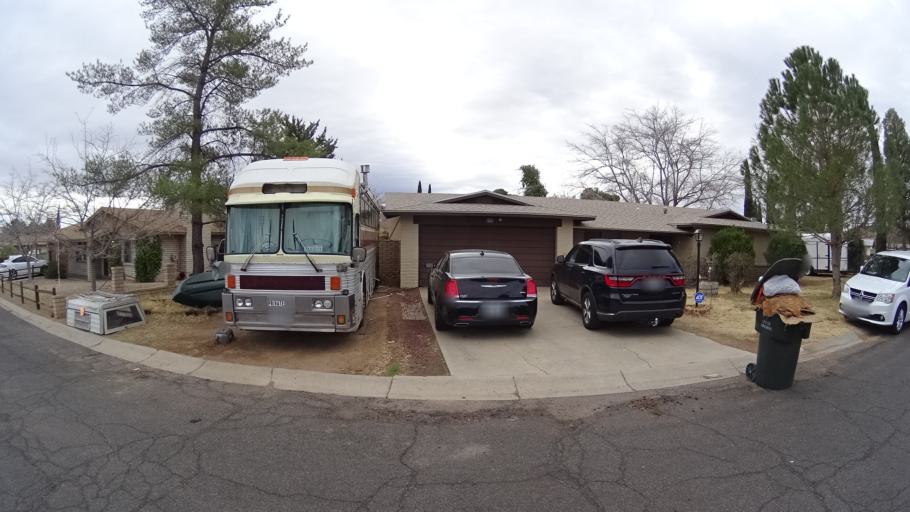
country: US
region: Arizona
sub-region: Mohave County
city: New Kingman-Butler
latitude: 35.2386
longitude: -114.0427
